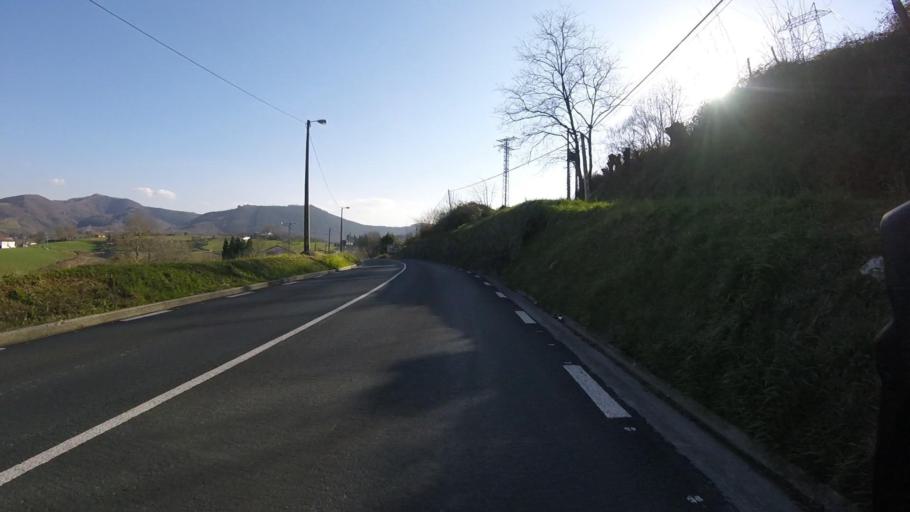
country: ES
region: Basque Country
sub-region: Provincia de Guipuzcoa
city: Errenteria
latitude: 43.2842
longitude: -1.9141
